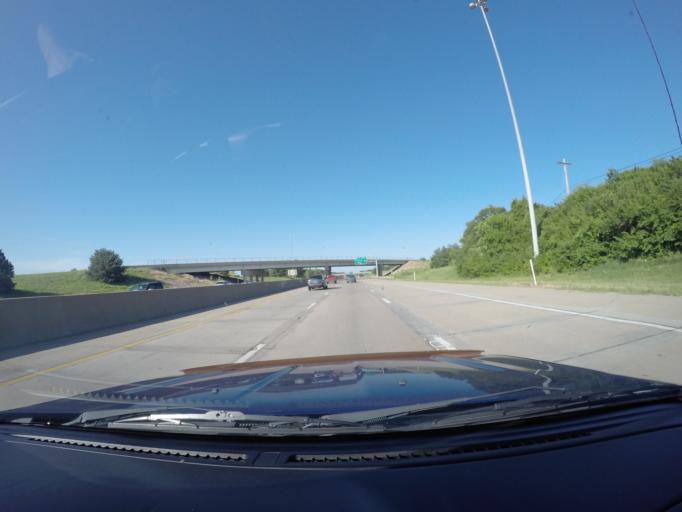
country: US
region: Kansas
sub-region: Shawnee County
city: Topeka
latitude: 39.0575
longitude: -95.7471
